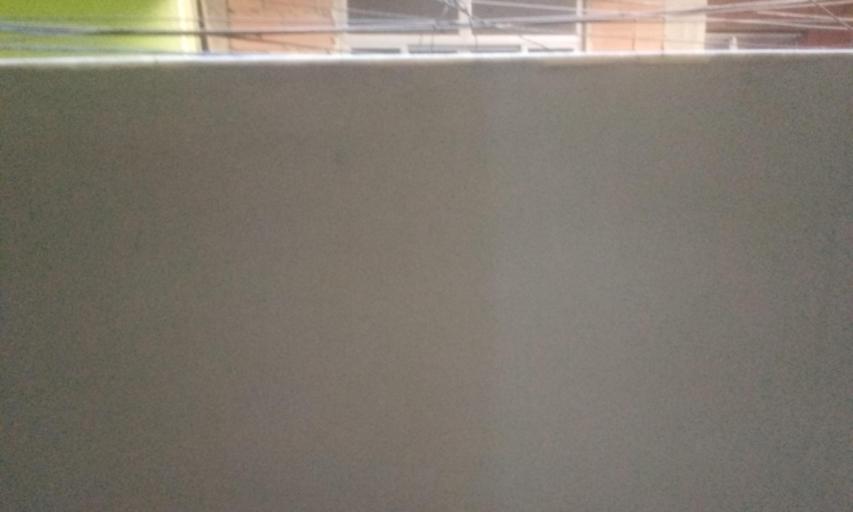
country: BR
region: Rio de Janeiro
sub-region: Rio De Janeiro
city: Rio de Janeiro
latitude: -22.9792
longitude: -43.3377
